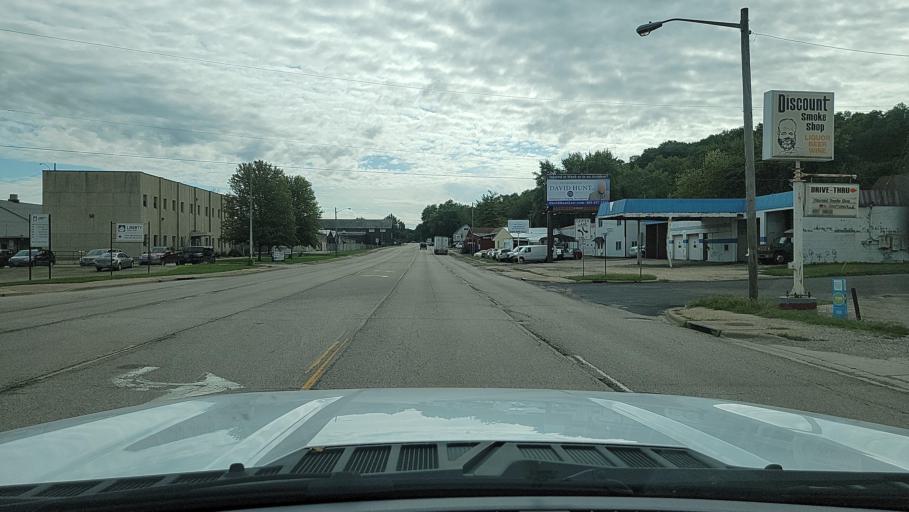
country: US
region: Illinois
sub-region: Peoria County
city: Bartonville
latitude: 40.6465
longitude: -89.6503
